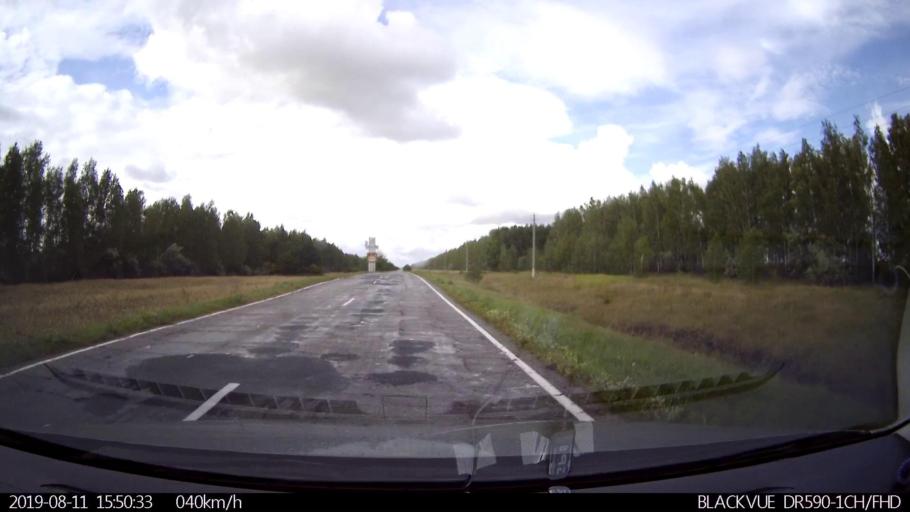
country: RU
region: Ulyanovsk
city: Ignatovka
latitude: 53.9127
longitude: 47.6558
